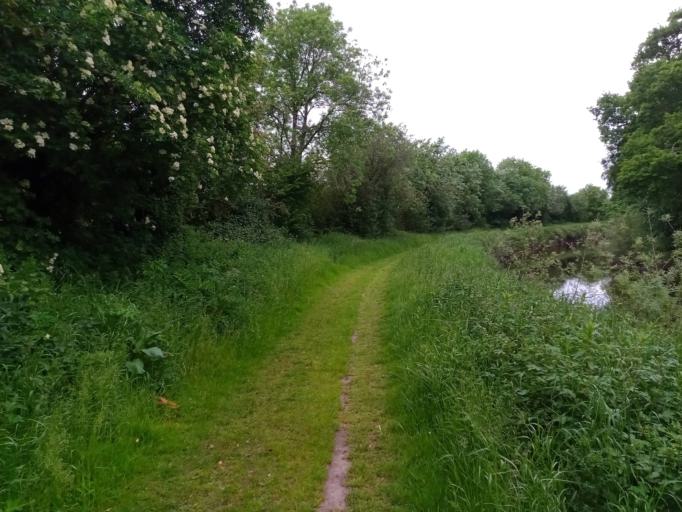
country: IE
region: Leinster
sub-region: County Carlow
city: Carlow
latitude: 52.8184
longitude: -6.9504
